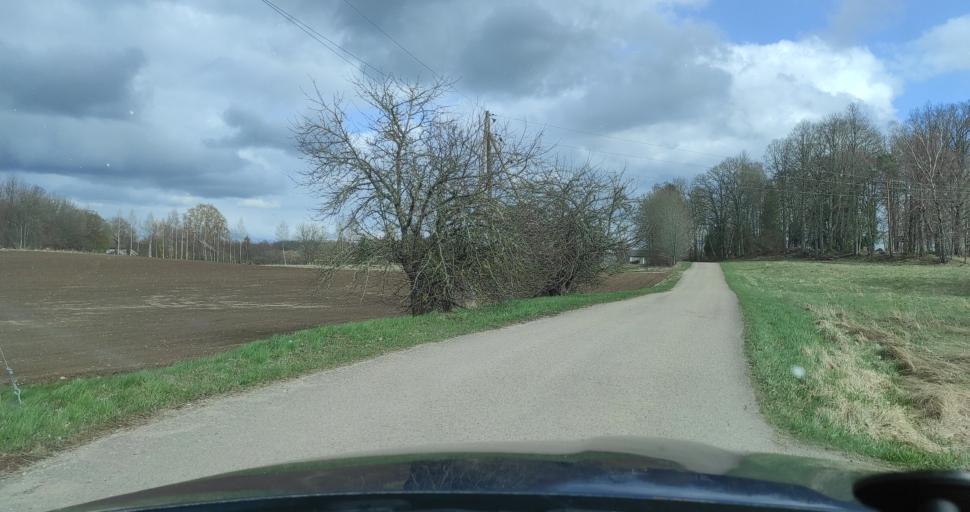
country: LV
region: Aizpute
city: Aizpute
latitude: 56.7124
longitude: 21.5771
